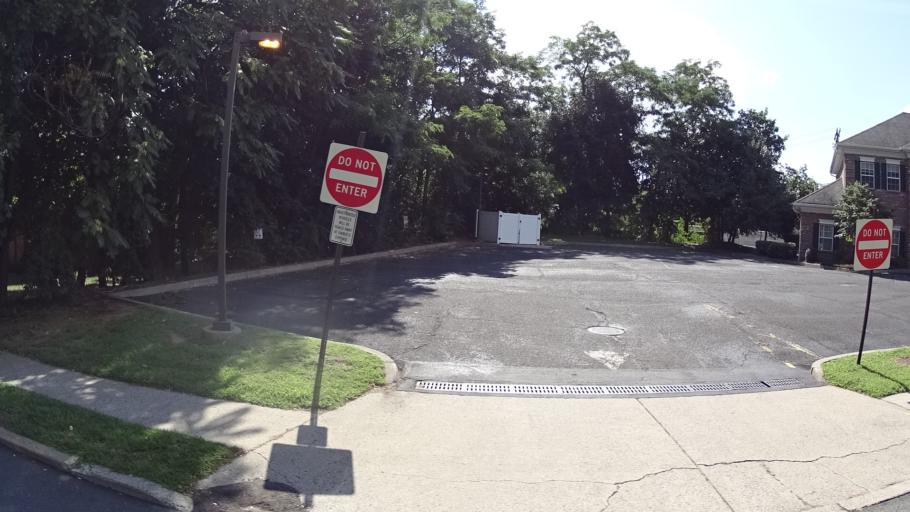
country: US
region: New Jersey
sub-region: Union County
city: New Providence
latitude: 40.7133
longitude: -74.3866
